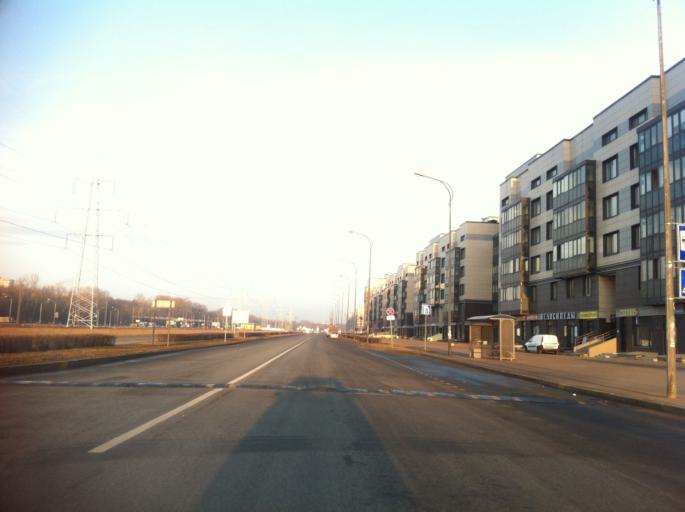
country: RU
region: St.-Petersburg
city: Sosnovaya Polyana
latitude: 59.8476
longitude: 30.1558
